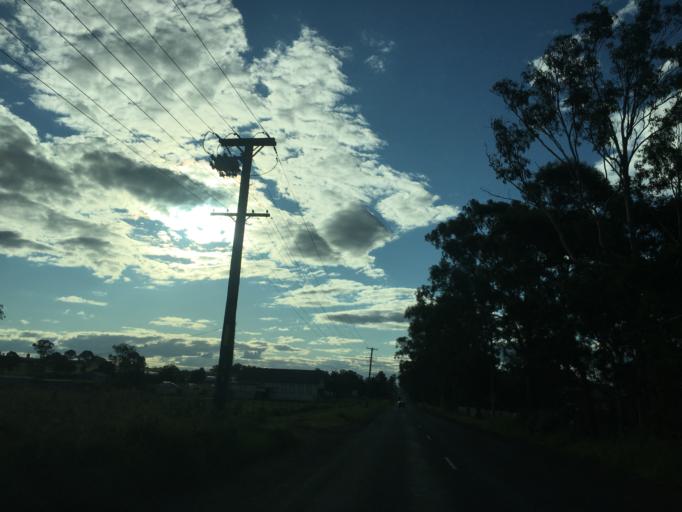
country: AU
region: New South Wales
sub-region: Campbelltown Municipality
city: Denham Court
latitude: -33.9624
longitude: 150.8054
